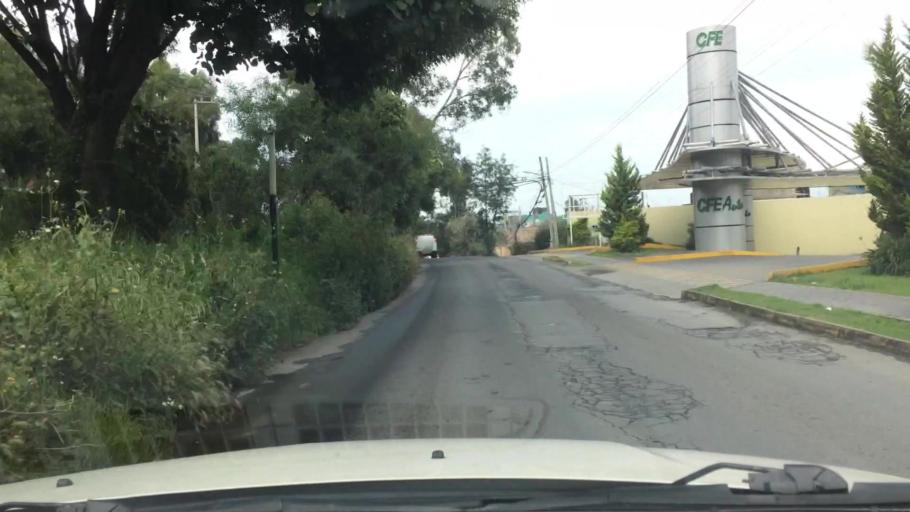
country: MX
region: Mexico City
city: Magdalena Contreras
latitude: 19.3392
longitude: -99.2093
